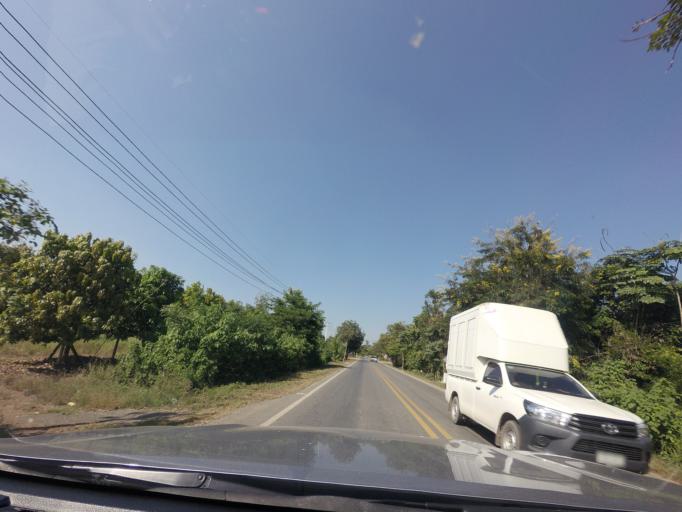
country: TH
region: Sukhothai
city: Sawankhalok
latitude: 17.3415
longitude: 99.8266
